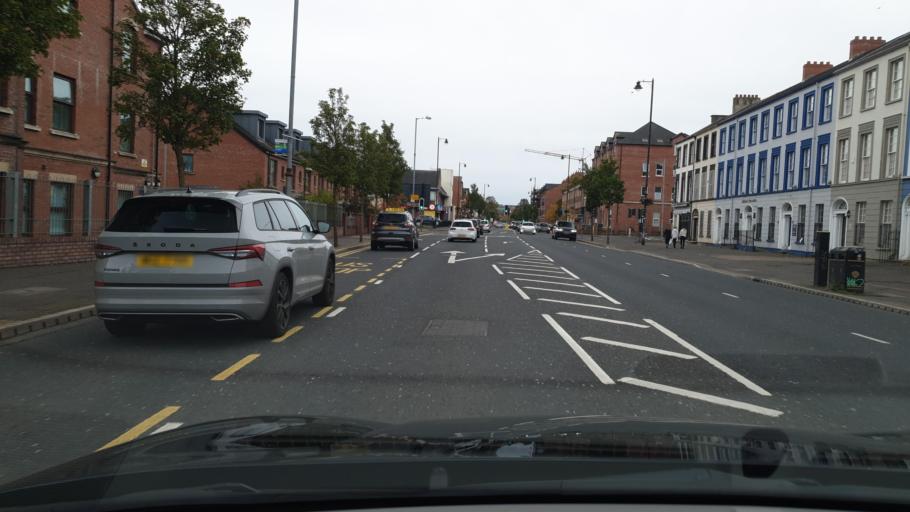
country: GB
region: Northern Ireland
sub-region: City of Belfast
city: Belfast
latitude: 54.5873
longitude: -5.9237
